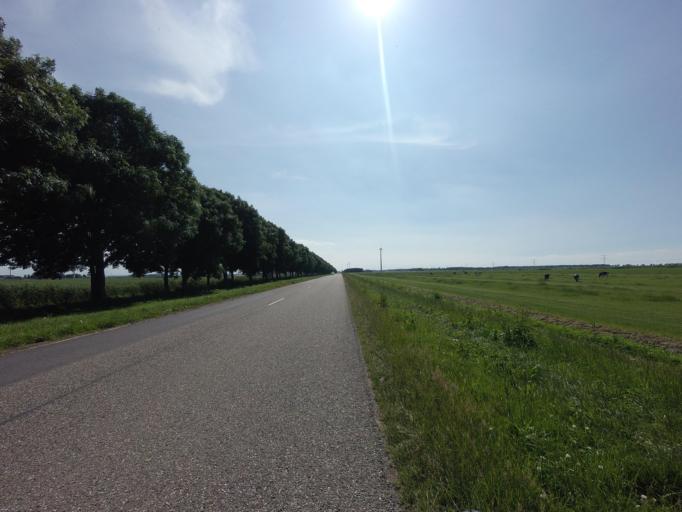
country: NL
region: Flevoland
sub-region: Gemeente Lelystad
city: Lelystad
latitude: 52.4151
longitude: 5.3970
